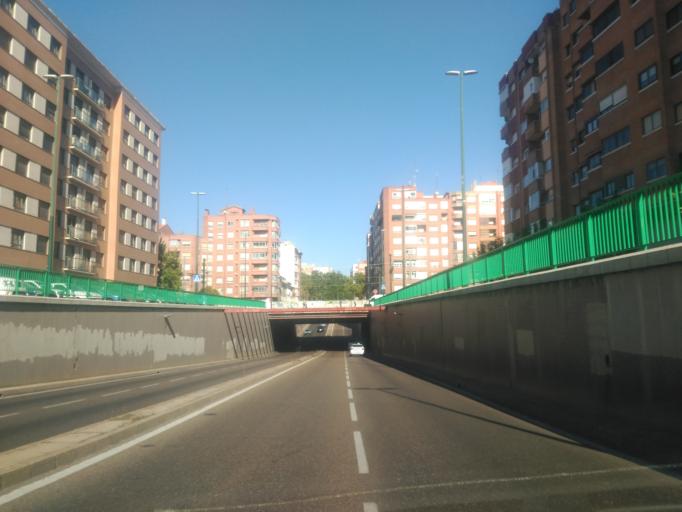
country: ES
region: Castille and Leon
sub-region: Provincia de Valladolid
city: Valladolid
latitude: 41.6451
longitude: -4.7151
